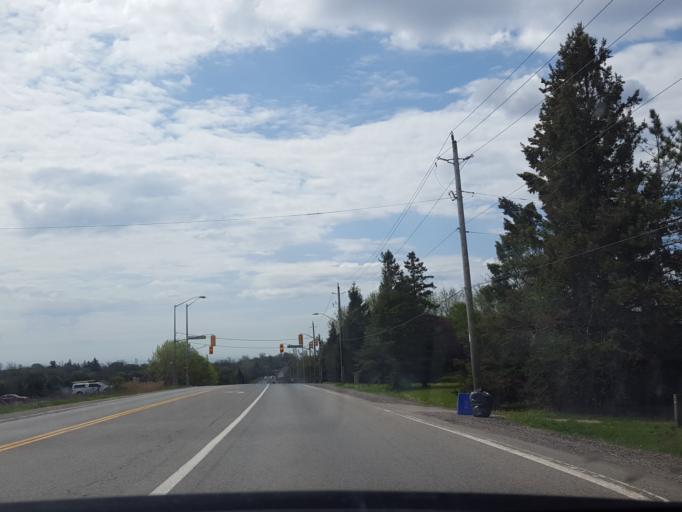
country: CA
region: Ontario
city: Oshawa
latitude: 43.9229
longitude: -78.7072
